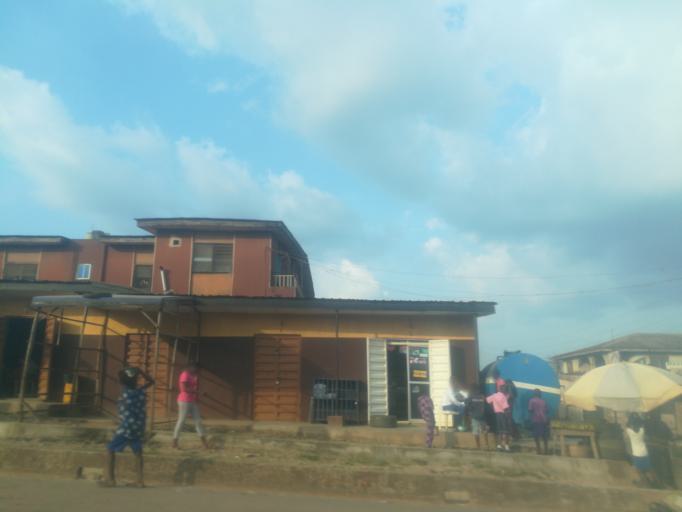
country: NG
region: Ogun
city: Abeokuta
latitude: 7.1665
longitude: 3.3044
